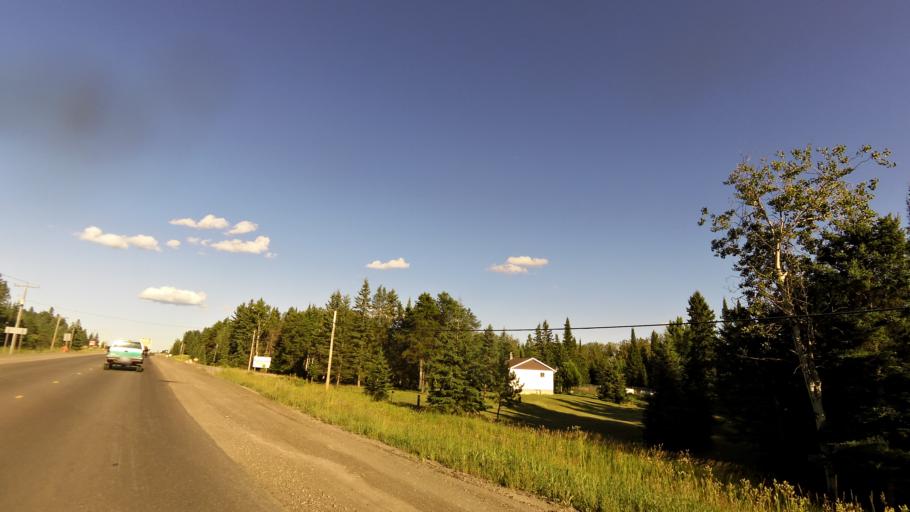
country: CA
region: Ontario
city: Dryden
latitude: 49.8151
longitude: -92.8695
